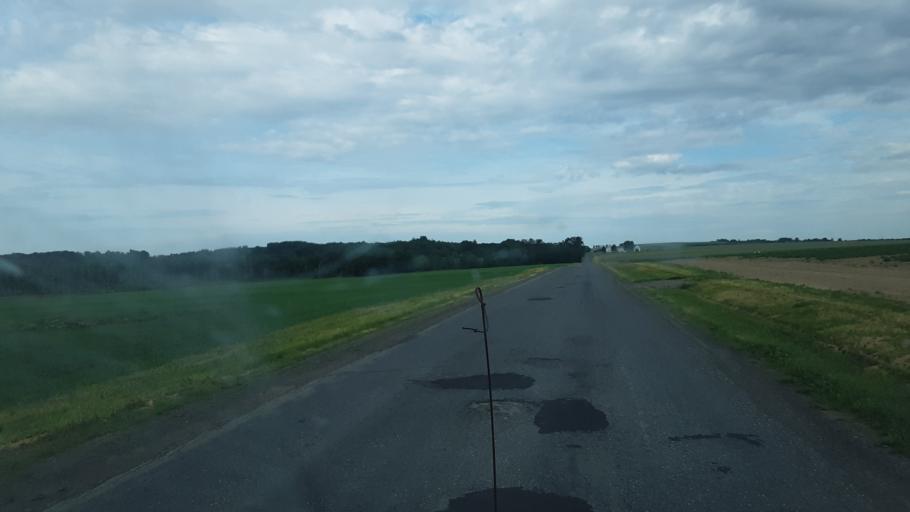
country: US
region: Maine
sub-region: Aroostook County
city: Caribou
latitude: 46.8115
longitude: -68.0020
